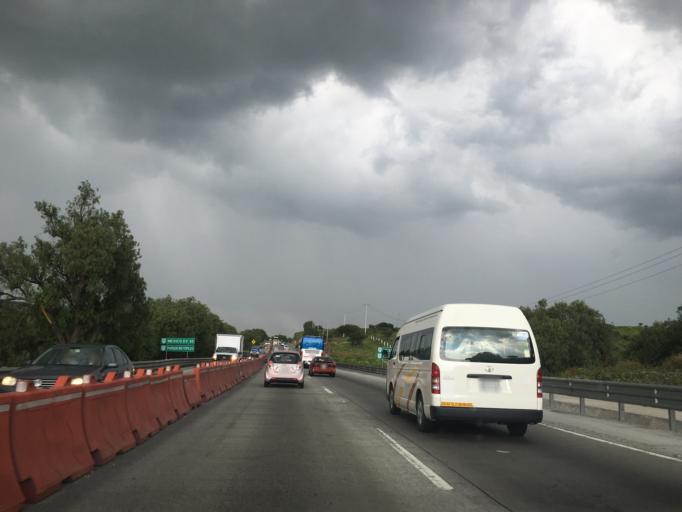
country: MX
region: Hidalgo
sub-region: Tepeji del Rio de Ocampo
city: Santiago Tlapanaloya
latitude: 19.8639
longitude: -99.3281
